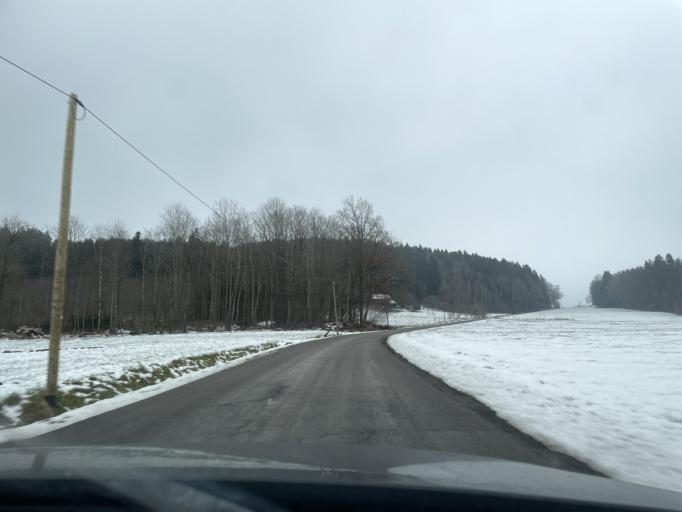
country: DE
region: Bavaria
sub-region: Lower Bavaria
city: Kollnburg
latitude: 49.0178
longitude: 12.8922
